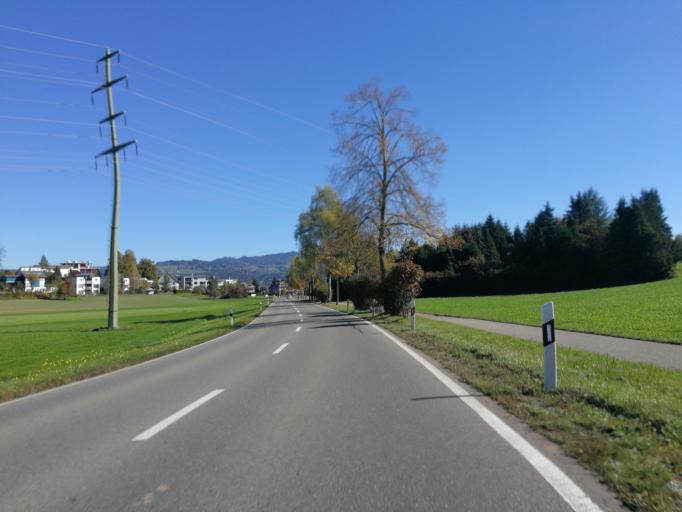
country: CH
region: Zurich
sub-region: Bezirk Hinwil
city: Gruet
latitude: 47.3112
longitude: 8.7880
